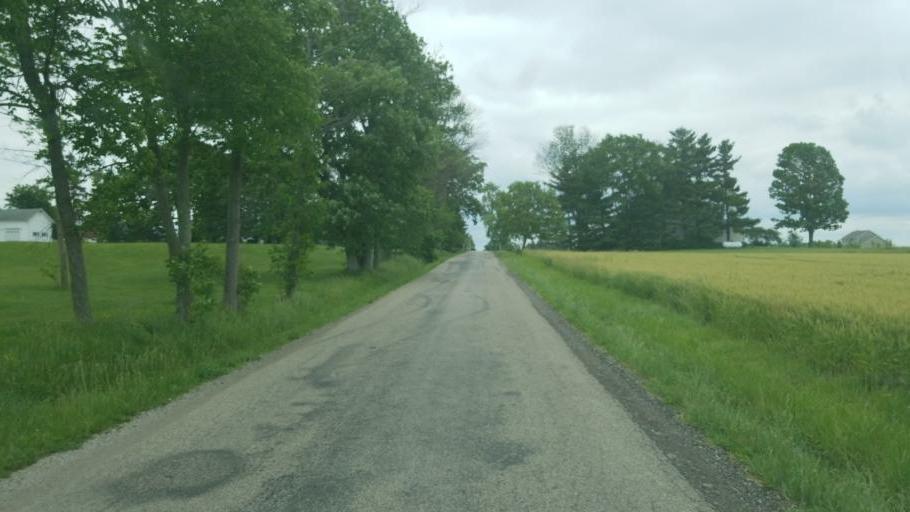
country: US
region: Ohio
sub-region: Fairfield County
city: Millersport
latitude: 39.8830
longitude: -82.5184
